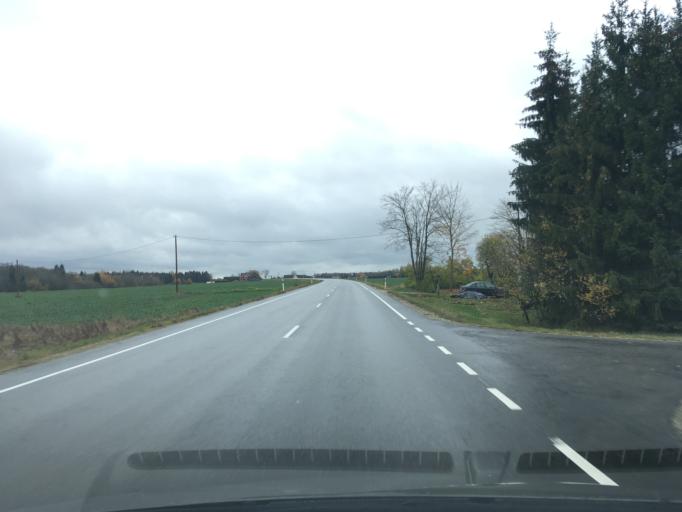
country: EE
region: Jogevamaa
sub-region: Tabivere vald
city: Tabivere
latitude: 58.4603
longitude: 26.5411
